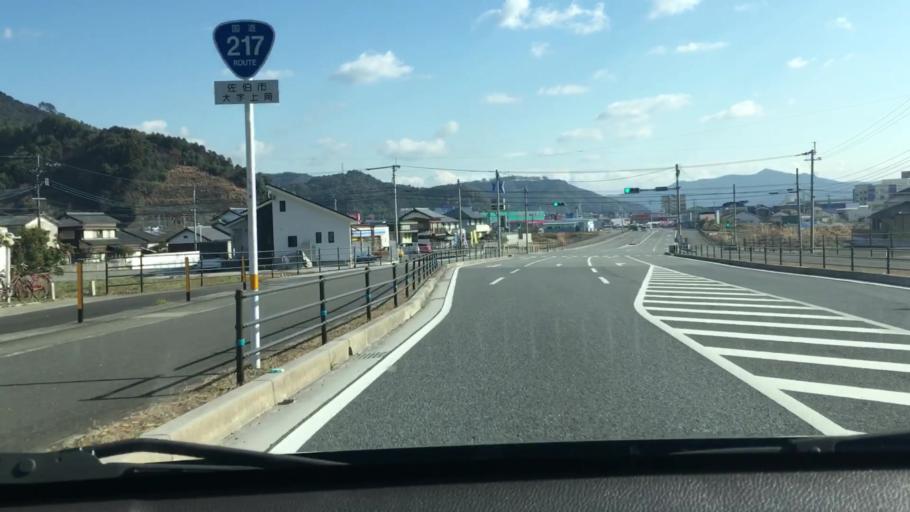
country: JP
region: Oita
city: Saiki
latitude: 32.9616
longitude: 131.8579
